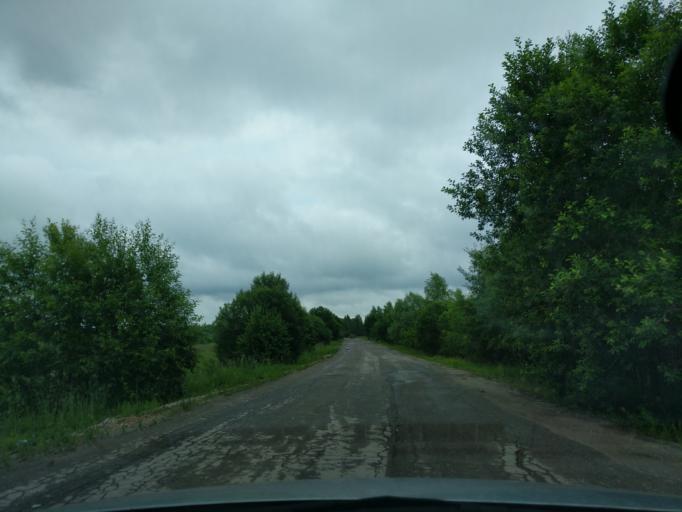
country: RU
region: Kaluga
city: Myatlevo
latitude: 54.8550
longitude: 35.5819
